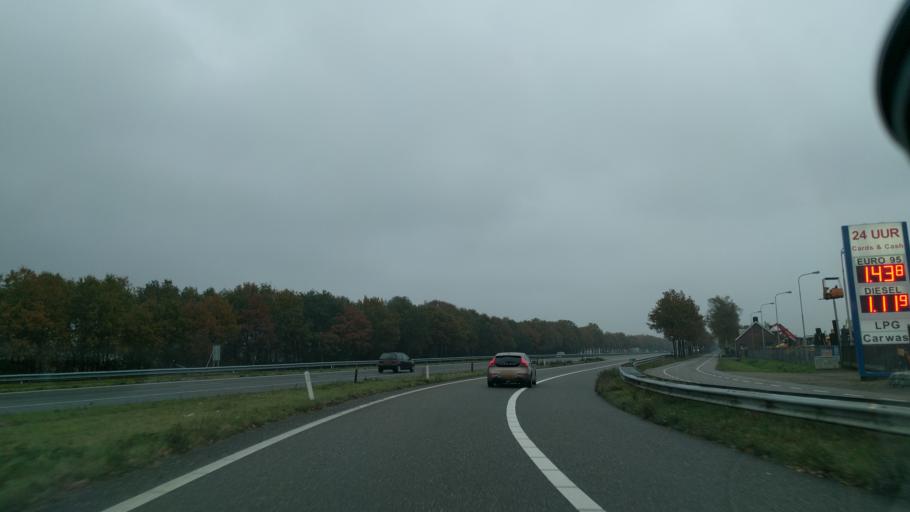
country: NL
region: North Brabant
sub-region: Gemeente Rucphen
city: Rucphen
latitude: 51.5514
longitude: 4.5473
